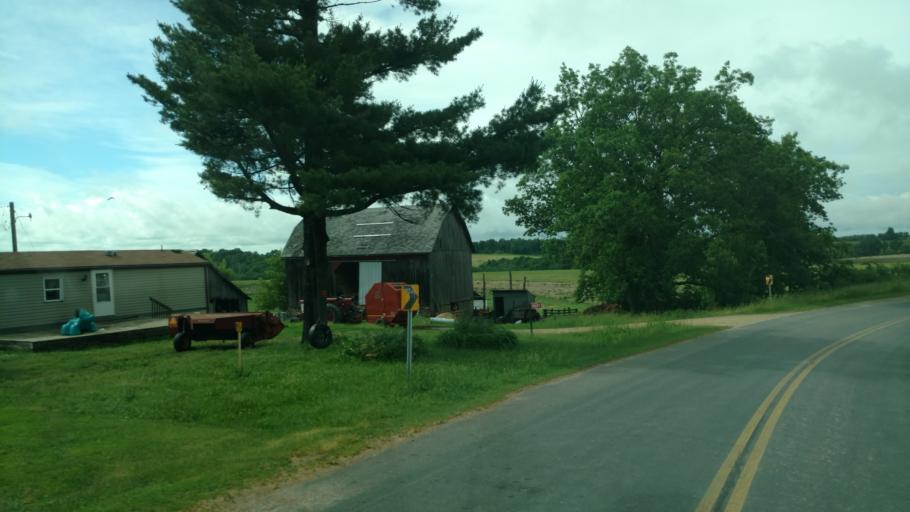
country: US
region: Wisconsin
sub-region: Vernon County
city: Hillsboro
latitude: 43.7324
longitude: -90.4479
